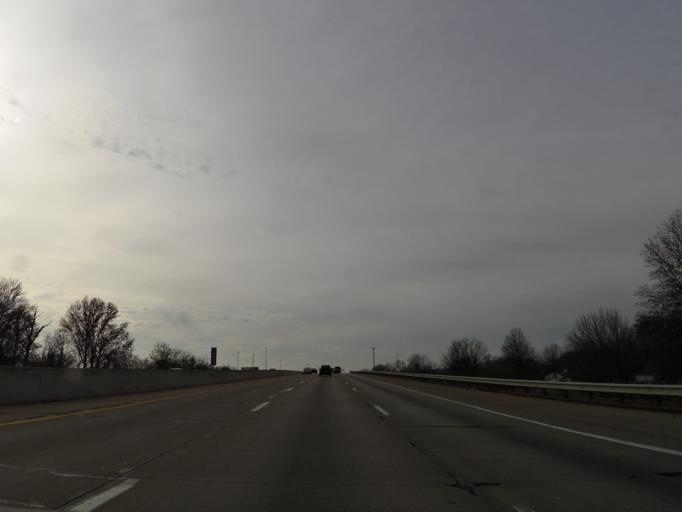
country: US
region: Indiana
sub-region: Marion County
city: Warren Park
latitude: 39.7557
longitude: -86.0302
